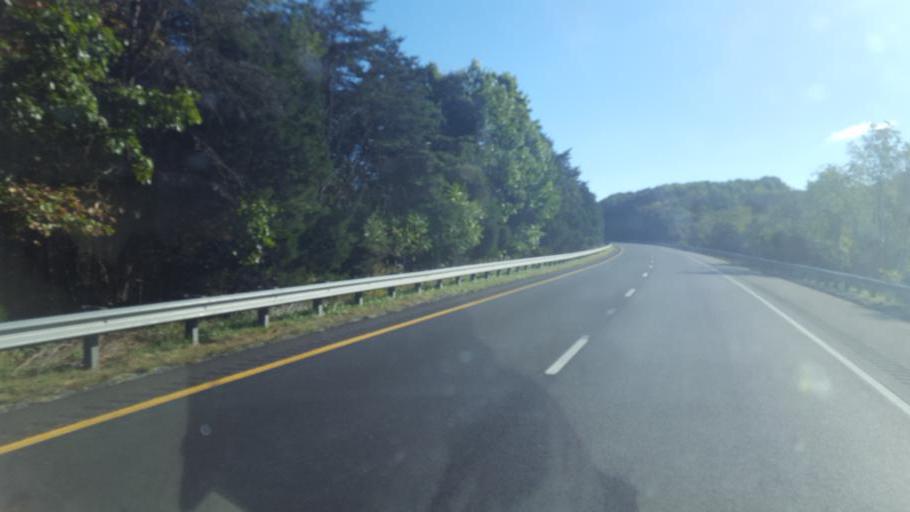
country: US
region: Maryland
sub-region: Washington County
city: Wilson-Conococheague
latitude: 39.6272
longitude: -77.9734
